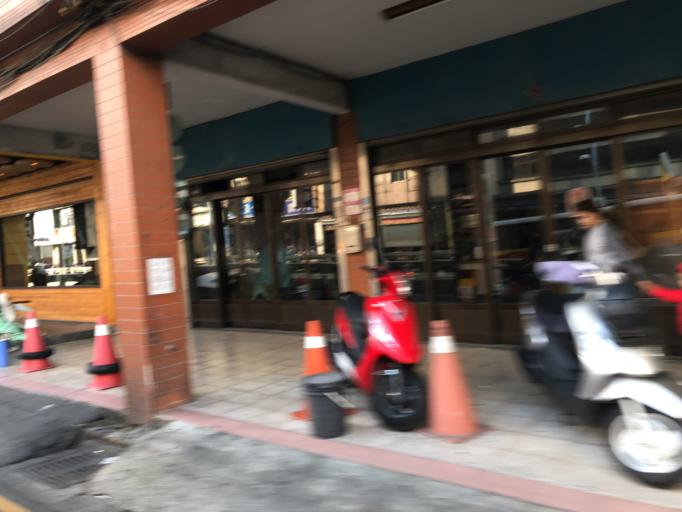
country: TW
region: Taiwan
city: Taoyuan City
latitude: 24.9550
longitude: 121.2264
